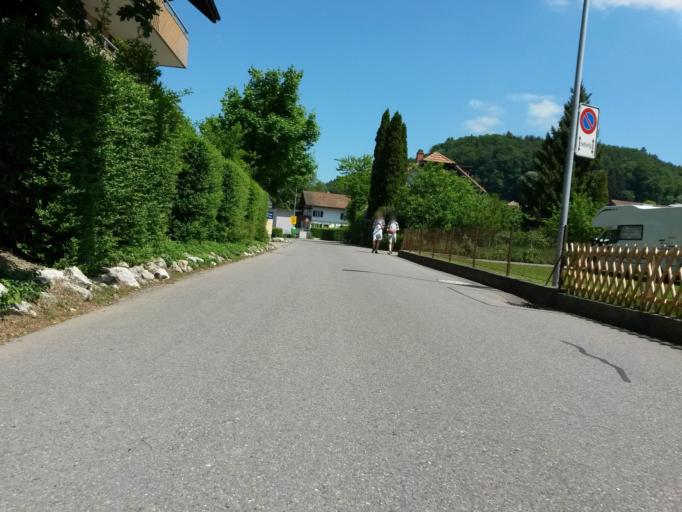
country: CH
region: Bern
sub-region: Biel/Bienne District
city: Orpund
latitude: 47.1205
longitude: 7.3380
